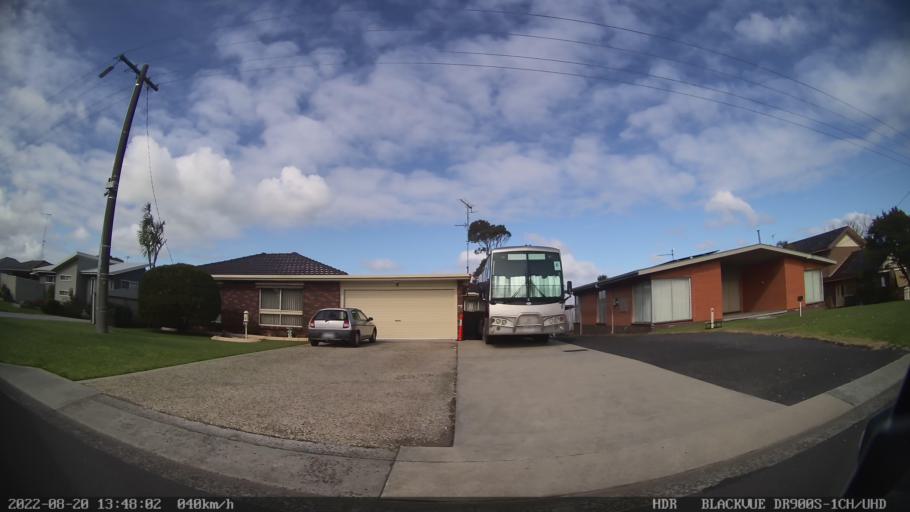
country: AU
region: Victoria
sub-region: Bass Coast
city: North Wonthaggi
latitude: -38.6041
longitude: 145.6013
